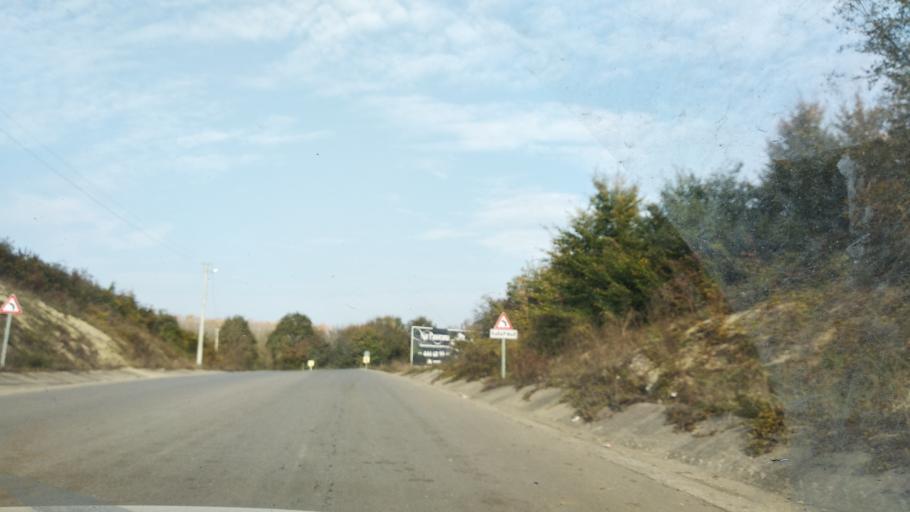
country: TR
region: Sakarya
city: Karasu
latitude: 41.0551
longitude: 30.6348
